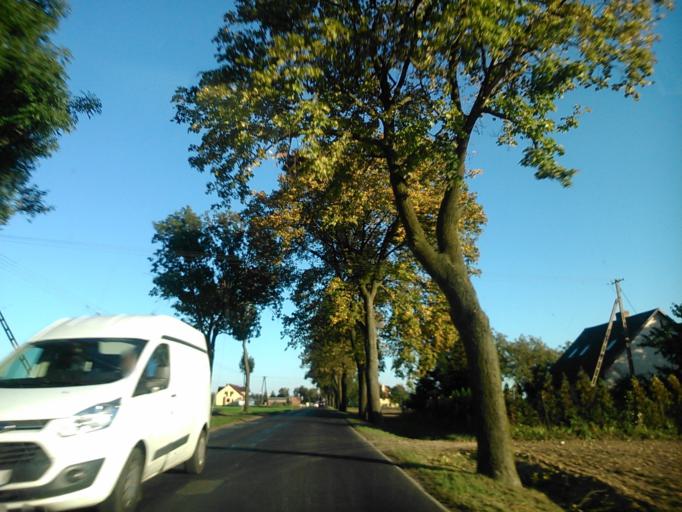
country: PL
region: Kujawsko-Pomorskie
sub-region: Powiat golubsko-dobrzynski
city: Golub-Dobrzyn
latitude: 53.1311
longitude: 19.0191
